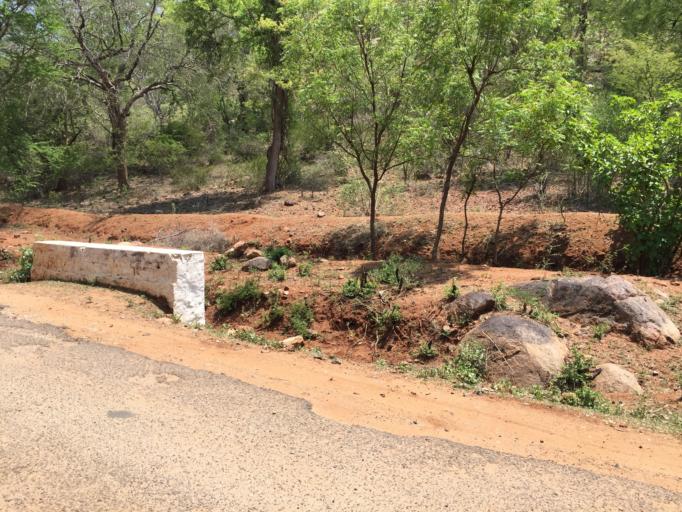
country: IN
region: Karnataka
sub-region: Chamrajnagar
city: Kollegal
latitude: 12.3053
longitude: 77.2951
